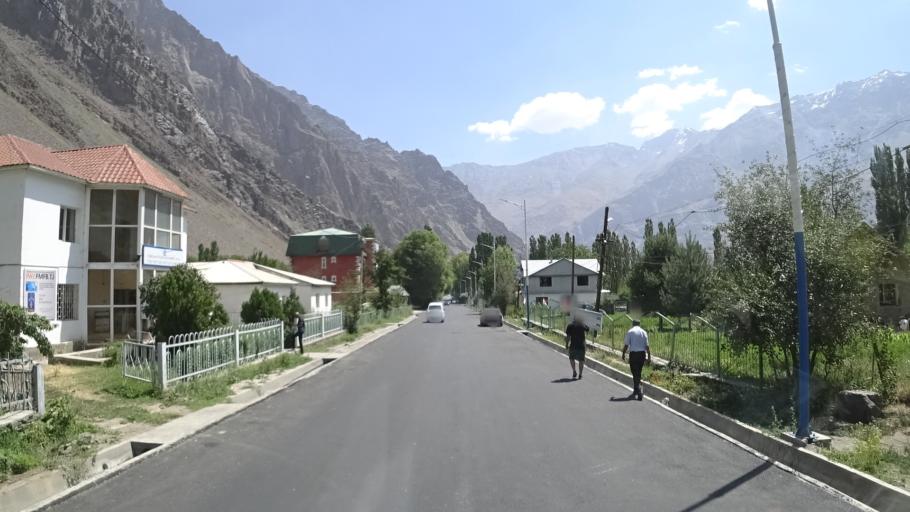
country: TJ
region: Gorno-Badakhshan
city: Rushon
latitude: 37.9463
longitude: 71.5656
